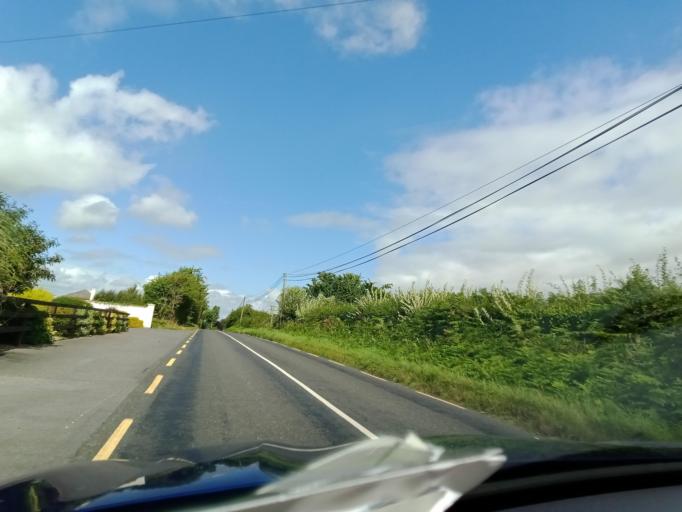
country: IE
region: Leinster
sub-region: Laois
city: Abbeyleix
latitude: 52.9319
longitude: -7.3235
